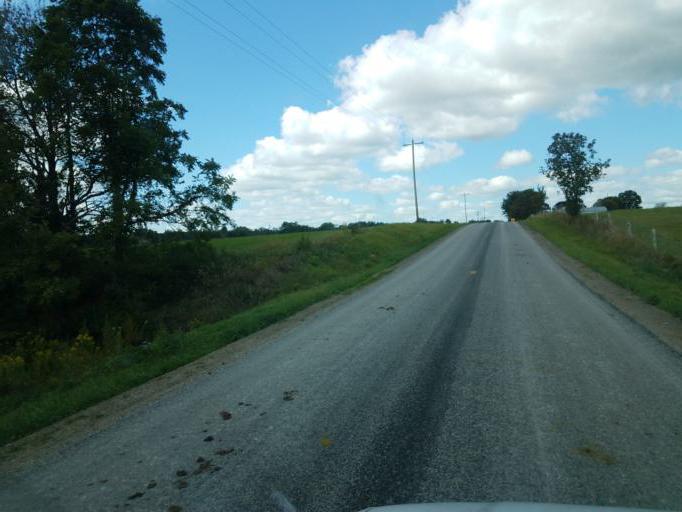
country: US
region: Ohio
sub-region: Wayne County
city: West Salem
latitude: 41.0425
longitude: -82.1214
